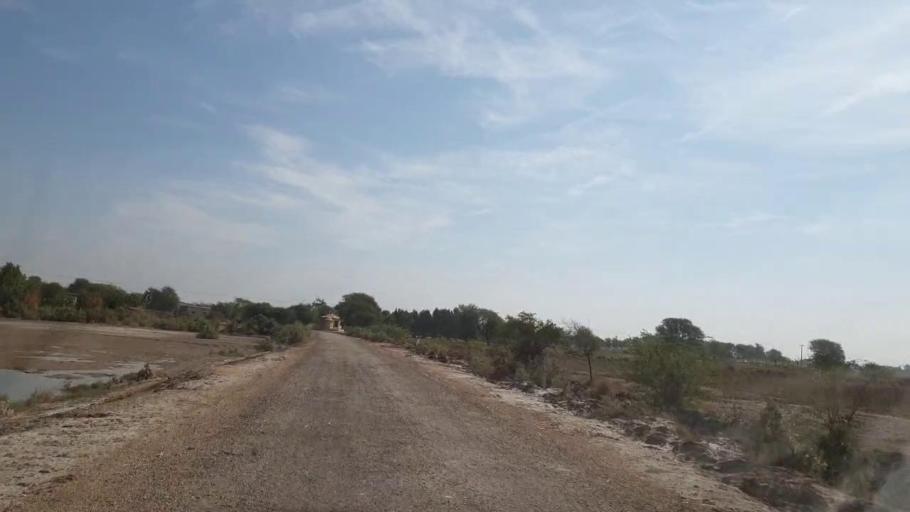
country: PK
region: Sindh
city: Mirpur Khas
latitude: 25.5346
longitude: 69.1586
